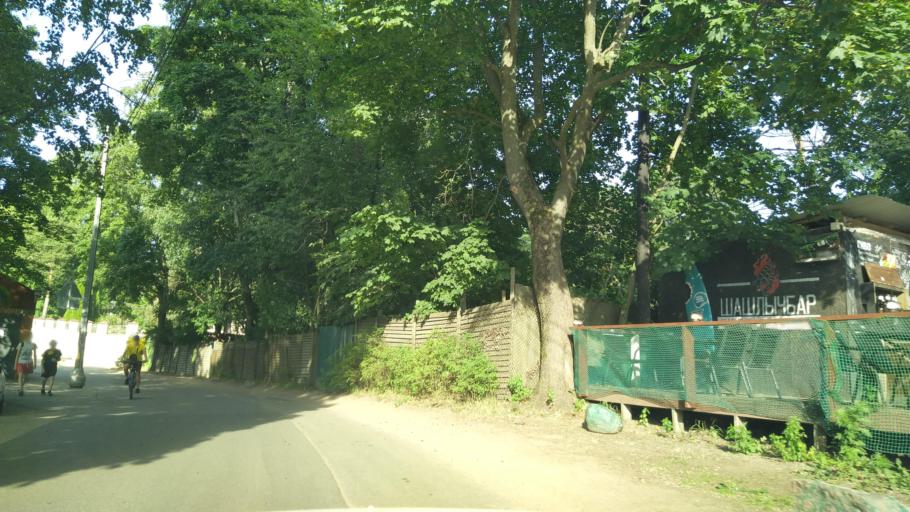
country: RU
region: St.-Petersburg
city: Ozerki
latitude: 60.0411
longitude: 30.3112
